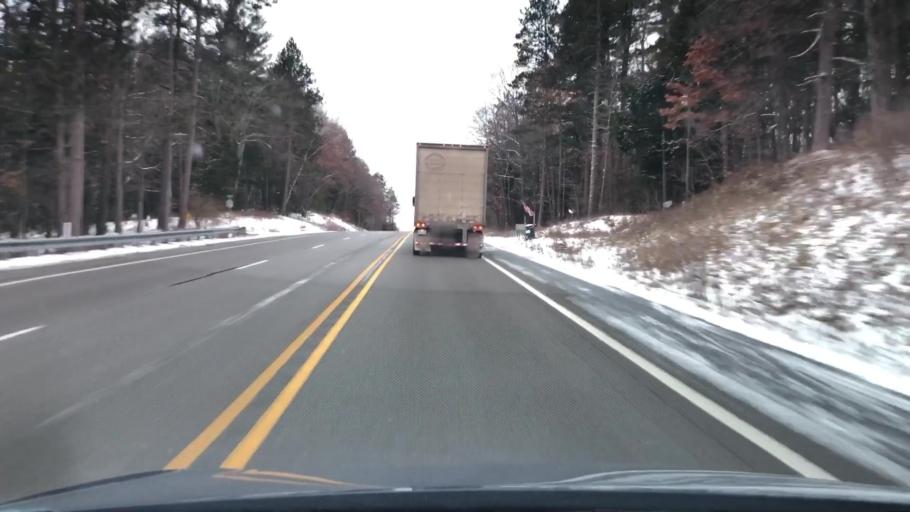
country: US
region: Michigan
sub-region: Wexford County
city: Cadillac
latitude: 44.1863
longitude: -85.3880
